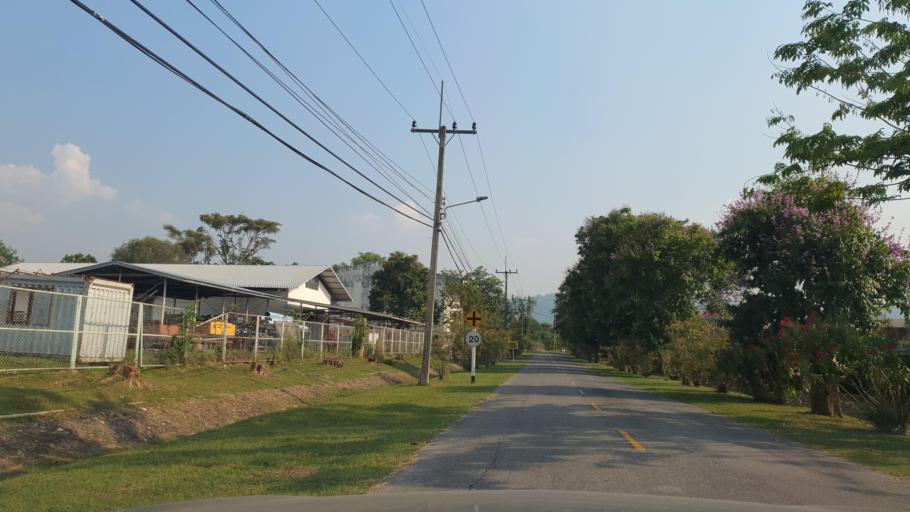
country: TH
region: Kanchanaburi
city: Sai Yok
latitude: 14.2287
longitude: 99.2349
